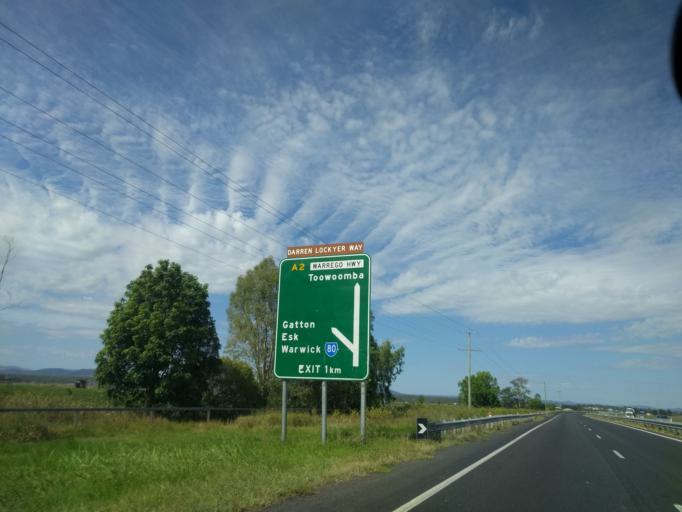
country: AU
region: Queensland
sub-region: Lockyer Valley
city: Gatton
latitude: -27.5497
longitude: 152.3284
